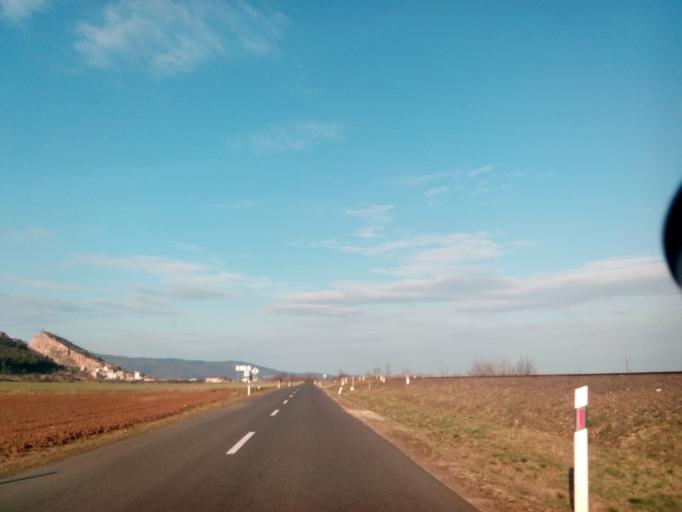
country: SK
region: Kosicky
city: Medzev
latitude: 48.5738
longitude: 20.8367
